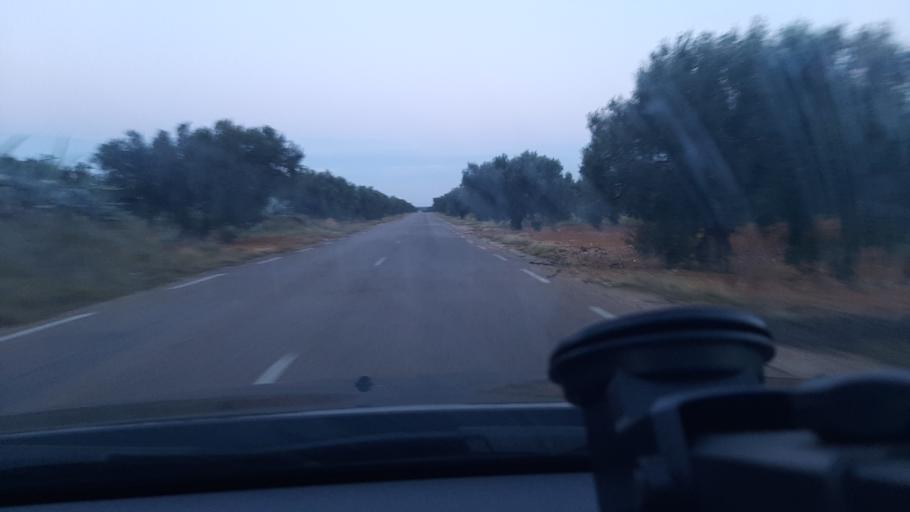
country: TN
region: Al Mahdiyah
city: Shurban
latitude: 35.0320
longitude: 10.5008
